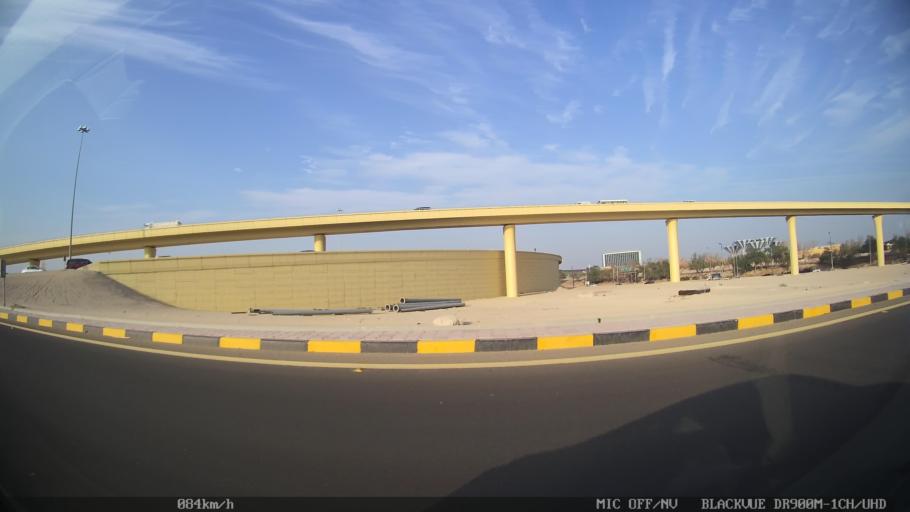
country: KW
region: Al Farwaniyah
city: Janub as Surrah
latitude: 29.2598
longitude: 47.9871
